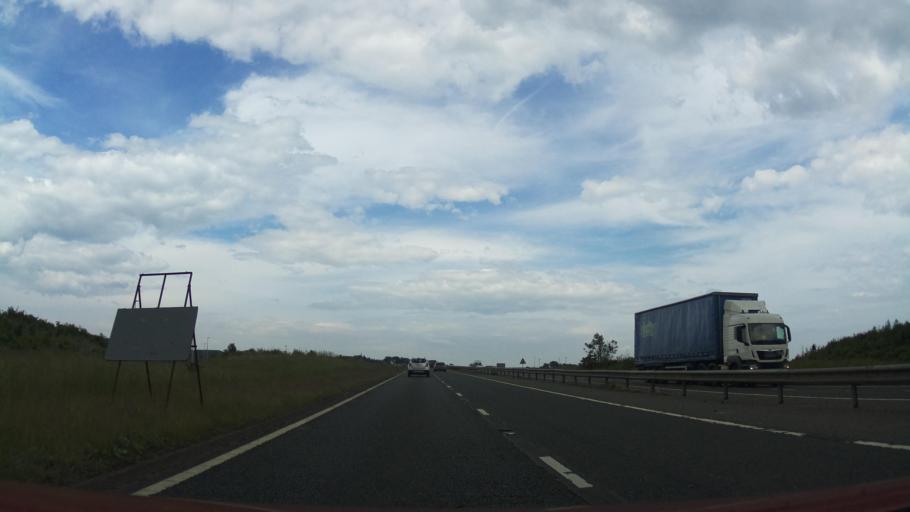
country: GB
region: England
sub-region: Northumberland
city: Morpeth
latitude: 55.1744
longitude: -1.7212
